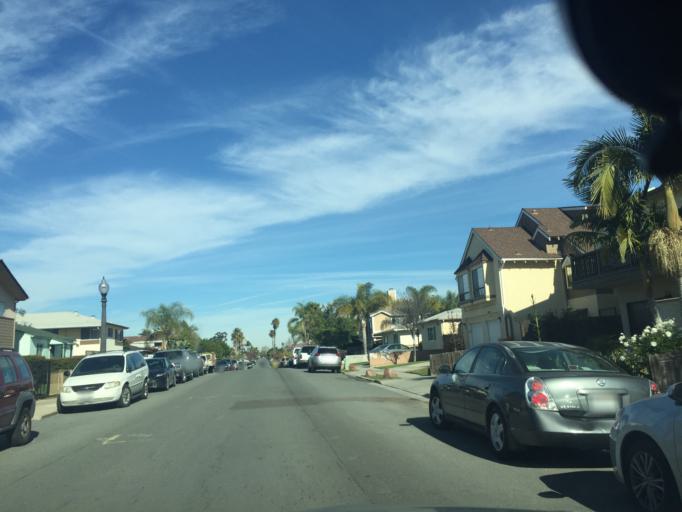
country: US
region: California
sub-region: San Diego County
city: Lemon Grove
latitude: 32.7574
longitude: -117.0879
